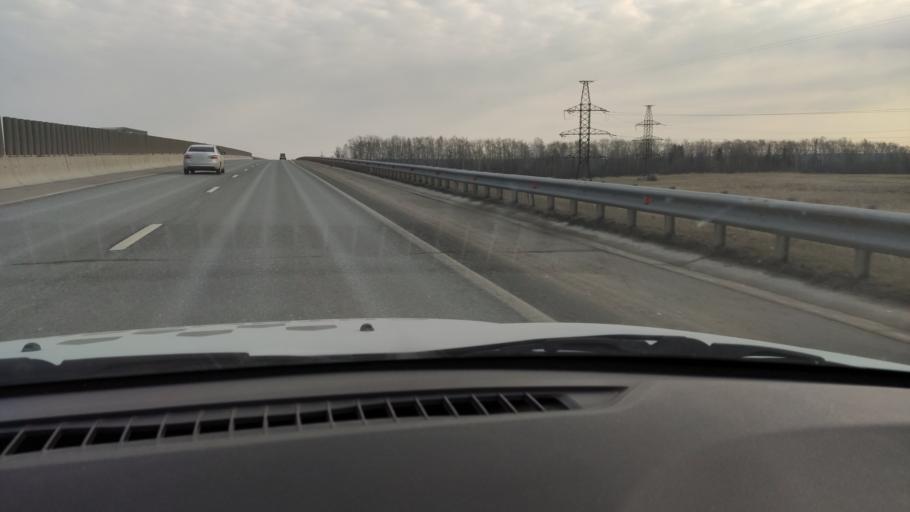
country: RU
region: Perm
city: Froly
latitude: 57.9311
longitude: 56.2899
